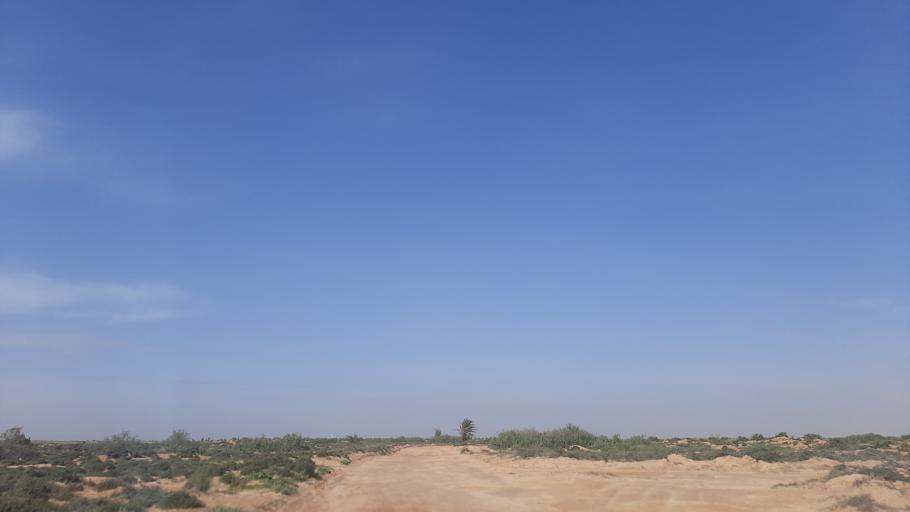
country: TN
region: Madanin
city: Zarzis
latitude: 33.4441
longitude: 10.8084
